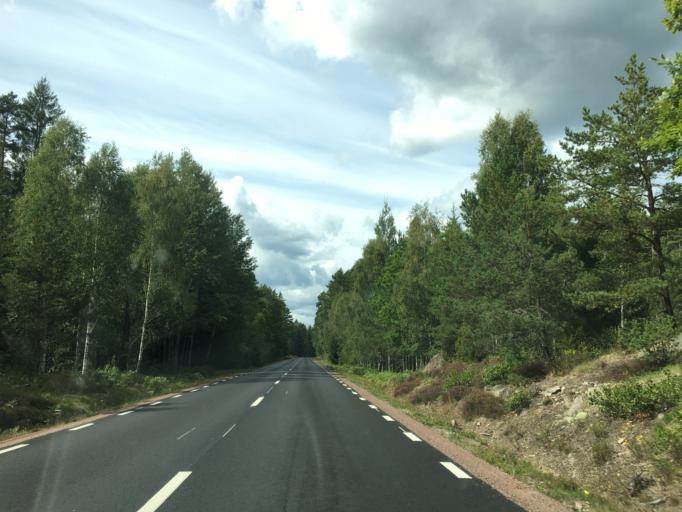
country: SE
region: Kalmar
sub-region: Nybro Kommun
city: Nybro
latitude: 56.9146
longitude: 16.0037
